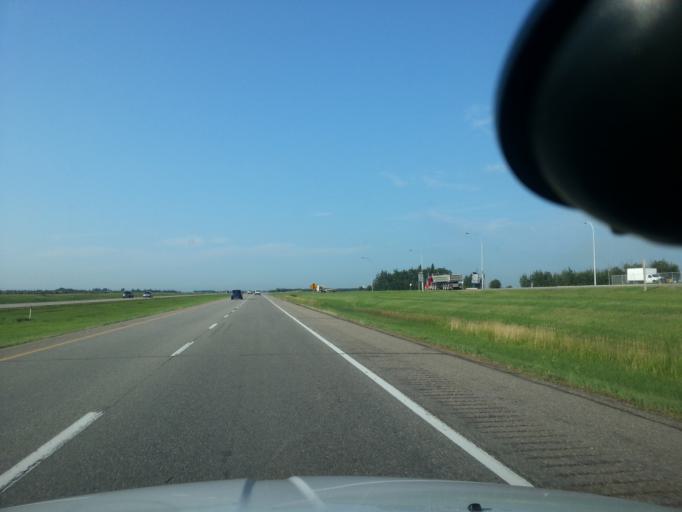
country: CA
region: Alberta
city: Leduc
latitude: 53.2323
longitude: -113.5710
